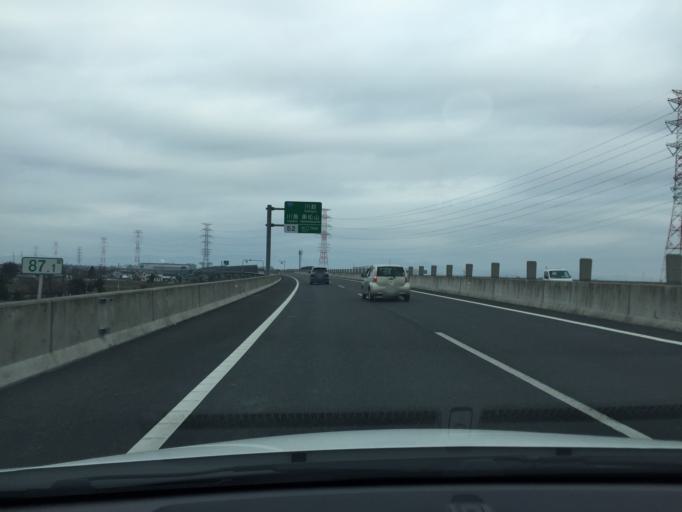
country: JP
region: Saitama
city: Kawagoe
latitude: 35.9857
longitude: 139.4787
